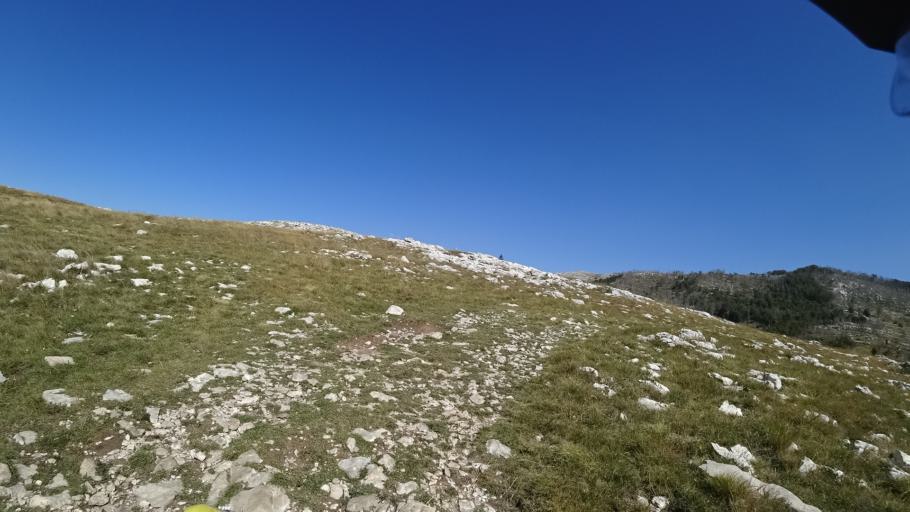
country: HR
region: Splitsko-Dalmatinska
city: Hrvace
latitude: 43.9128
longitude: 16.6087
